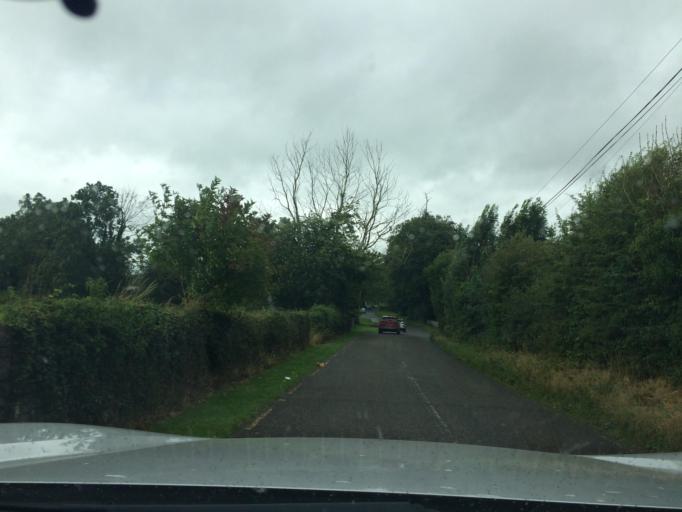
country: IE
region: Munster
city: Thurles
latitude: 52.6288
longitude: -7.8722
